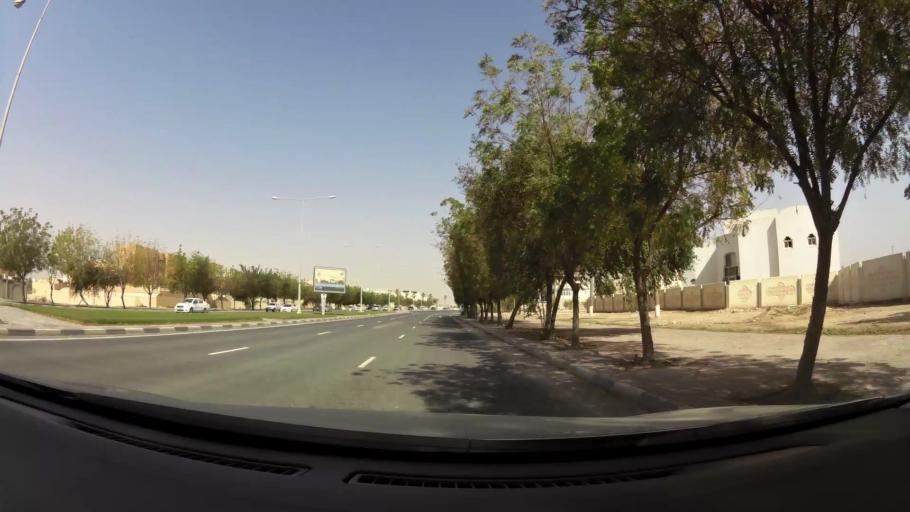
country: QA
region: Baladiyat ad Dawhah
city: Doha
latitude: 25.3534
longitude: 51.4975
